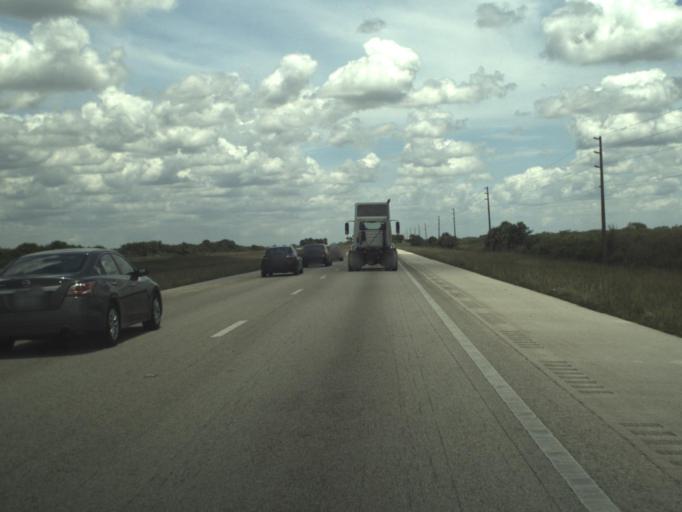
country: US
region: Florida
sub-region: Broward County
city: Weston
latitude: 26.1569
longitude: -80.7680
